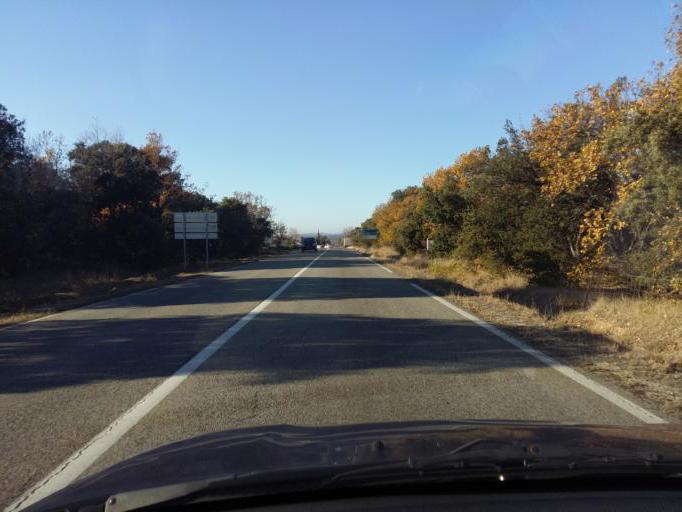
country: FR
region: Rhone-Alpes
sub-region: Departement de la Drome
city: Grignan
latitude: 44.4198
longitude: 4.8958
